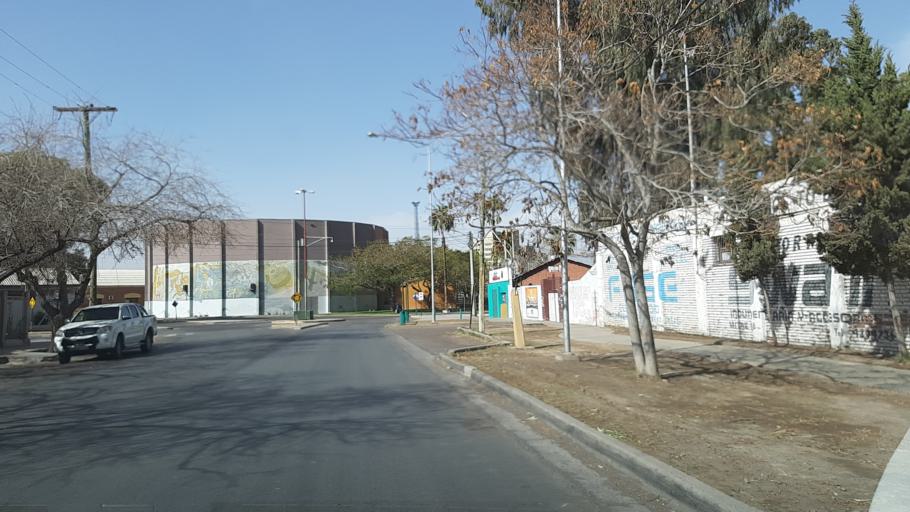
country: AR
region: San Juan
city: San Juan
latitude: -31.5320
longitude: -68.5395
